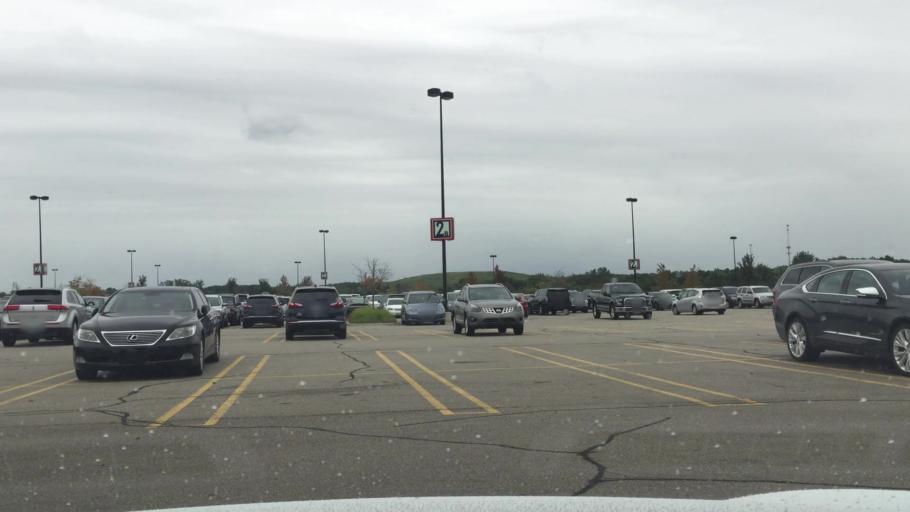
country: US
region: Michigan
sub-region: Oakland County
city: Pontiac
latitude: 42.7014
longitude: -83.3045
